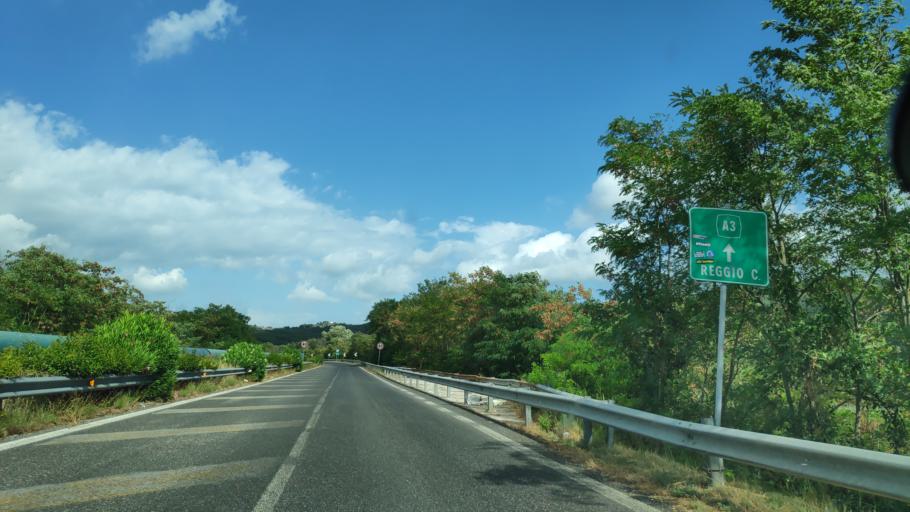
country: IT
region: Campania
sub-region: Provincia di Salerno
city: Serre
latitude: 40.6159
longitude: 15.1740
